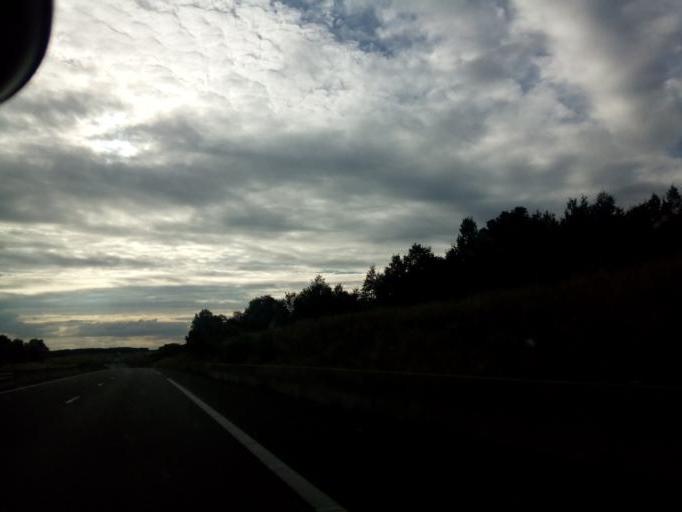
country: FR
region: Centre
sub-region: Departement d'Indre-et-Loire
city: Monts
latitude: 47.3070
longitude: 0.6570
